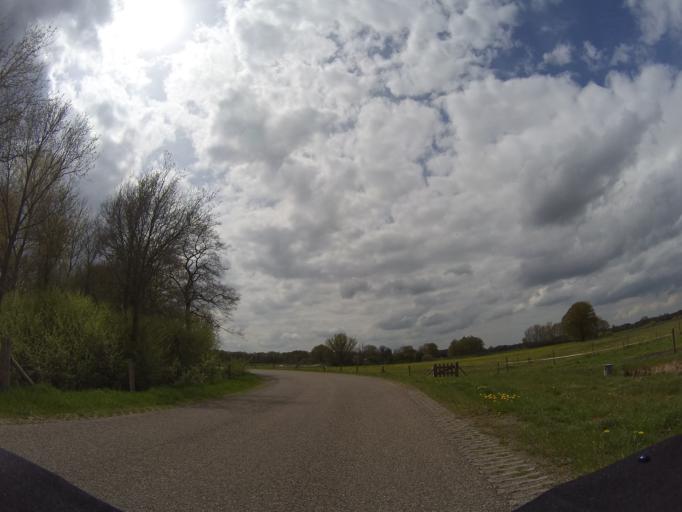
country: NL
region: Overijssel
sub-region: Gemeente Twenterand
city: Magele
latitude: 52.5295
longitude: 6.5039
